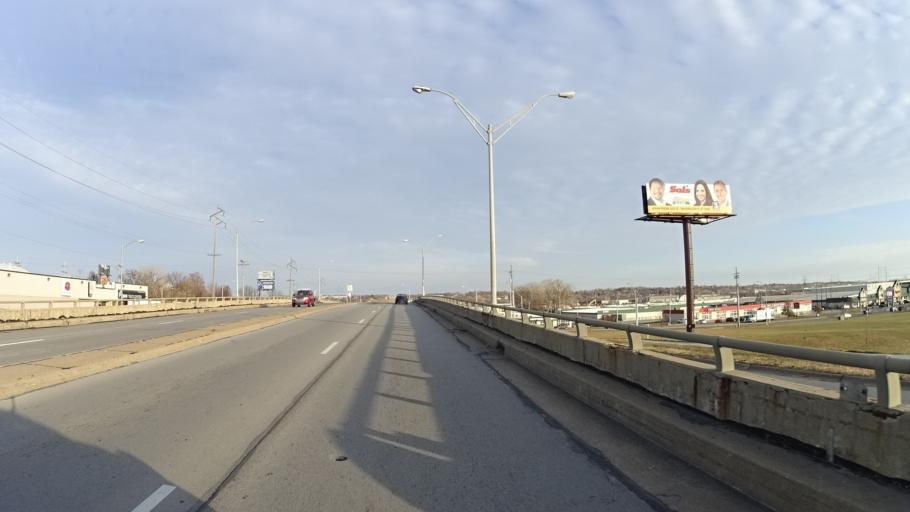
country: US
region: Nebraska
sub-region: Douglas County
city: Ralston
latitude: 41.2125
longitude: -96.0258
